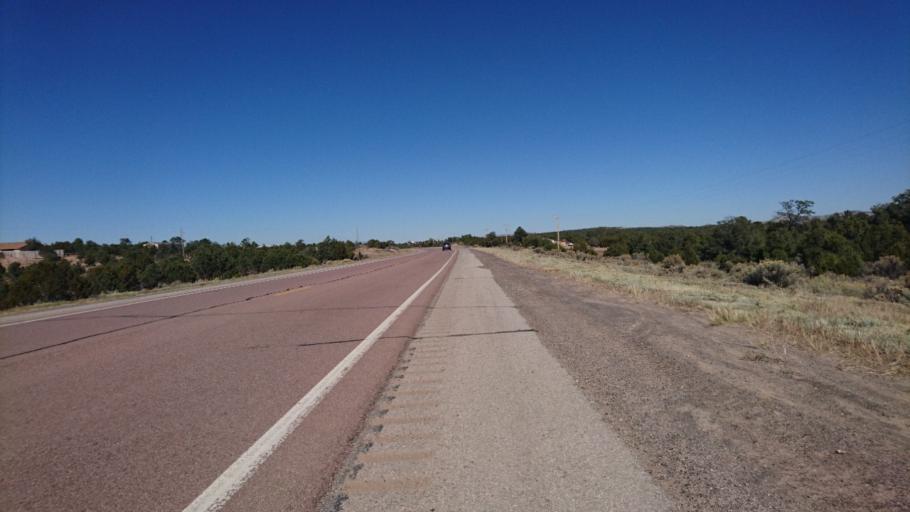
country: US
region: New Mexico
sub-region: McKinley County
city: Gallup
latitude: 35.3704
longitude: -108.7534
